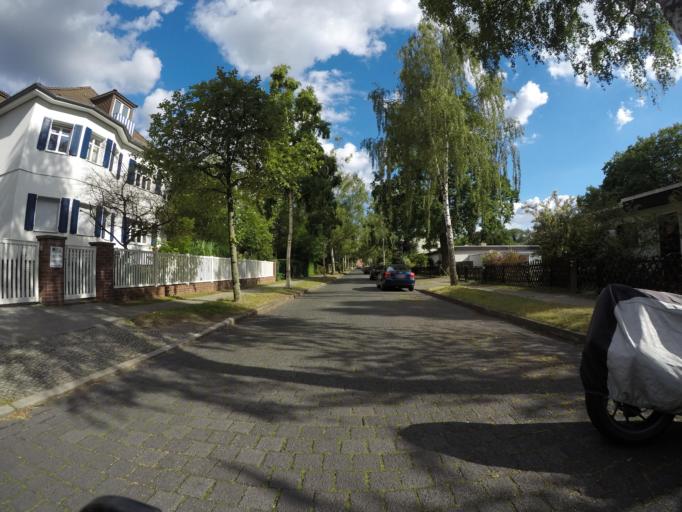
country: DE
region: Berlin
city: Zehlendorf Bezirk
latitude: 52.4269
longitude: 13.2671
